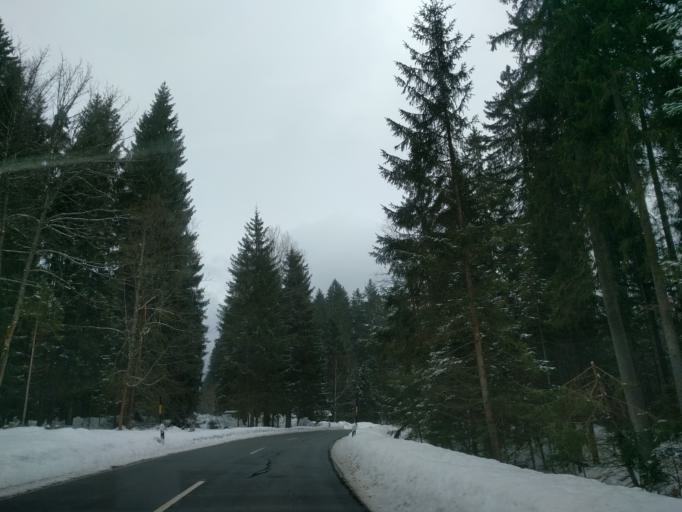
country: DE
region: Bavaria
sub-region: Lower Bavaria
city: Lindberg
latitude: 49.0543
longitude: 13.2878
